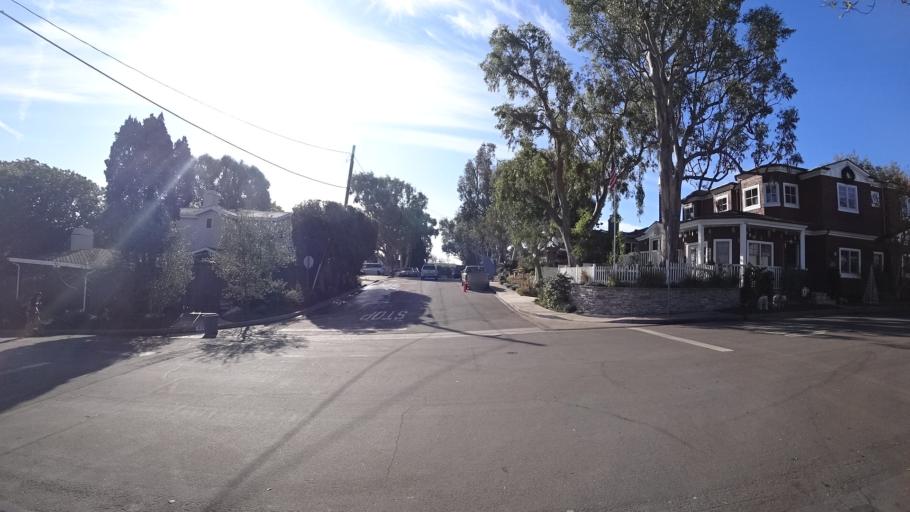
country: US
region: California
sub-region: Los Angeles County
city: Manhattan Beach
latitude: 33.8924
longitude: -118.4024
